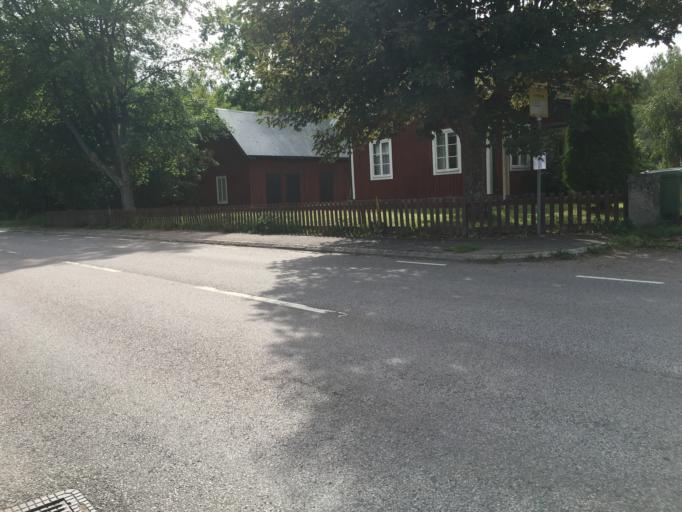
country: SE
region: Kalmar
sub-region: Nybro Kommun
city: Nybro
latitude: 56.9391
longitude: 15.9137
